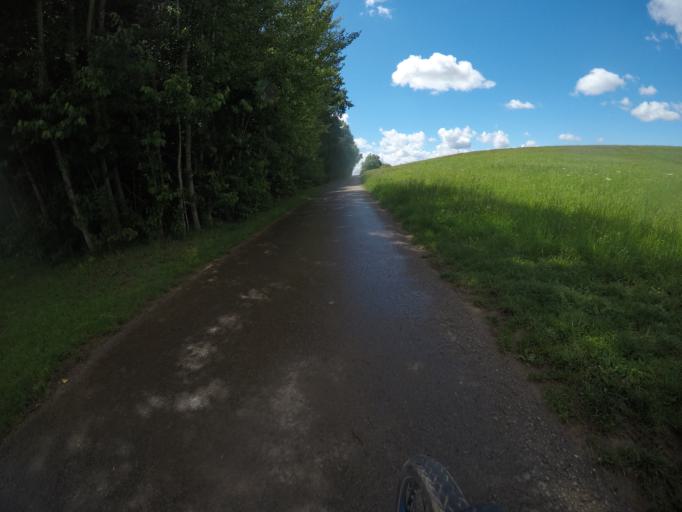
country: DE
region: Baden-Wuerttemberg
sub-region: Regierungsbezirk Stuttgart
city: Motzingen
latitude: 48.5010
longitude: 8.7485
